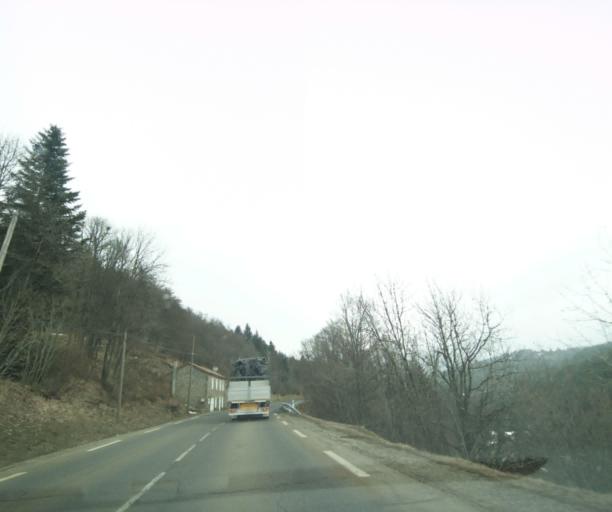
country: FR
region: Languedoc-Roussillon
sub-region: Departement de la Lozere
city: Langogne
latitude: 44.7198
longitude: 4.0071
